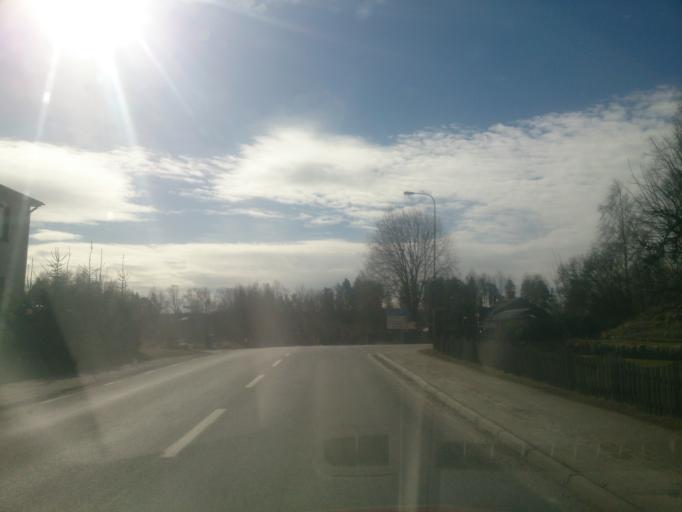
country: SE
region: OEstergoetland
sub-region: Finspangs Kommun
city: Finspang
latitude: 58.6790
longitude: 15.7516
